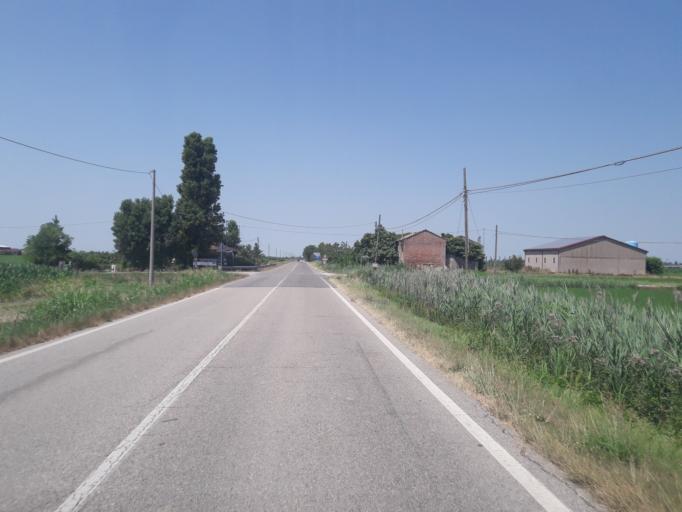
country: IT
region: Veneto
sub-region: Provincia di Rovigo
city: Papozze
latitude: 45.0054
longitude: 12.1655
